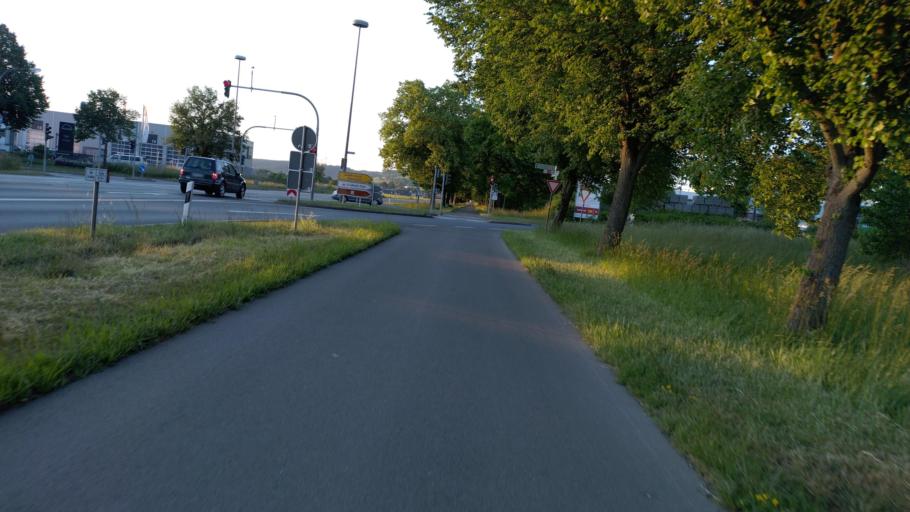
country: DE
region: Bavaria
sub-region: Upper Franconia
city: Bindlach
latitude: 49.9685
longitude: 11.6099
